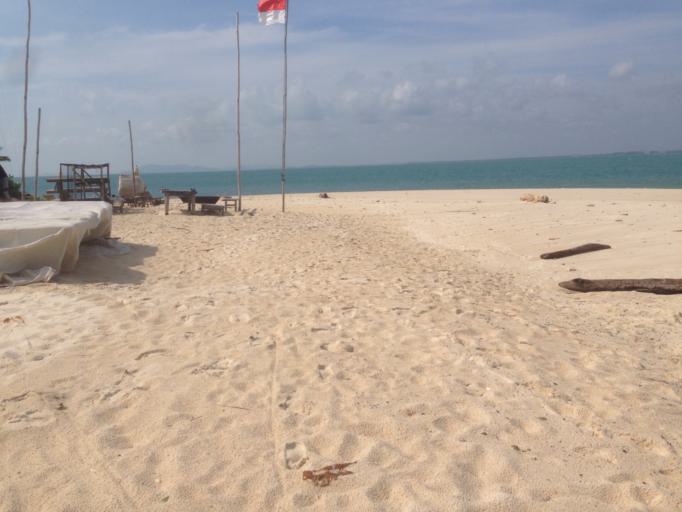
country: ID
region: Riau Islands
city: Kijang
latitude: 1.0520
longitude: 104.7069
